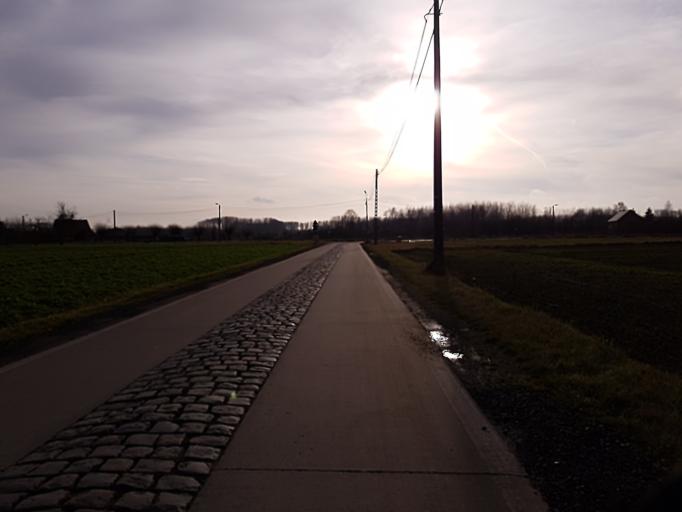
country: BE
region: Flanders
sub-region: Provincie Vlaams-Brabant
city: Rotselaar
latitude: 50.9598
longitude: 4.6915
